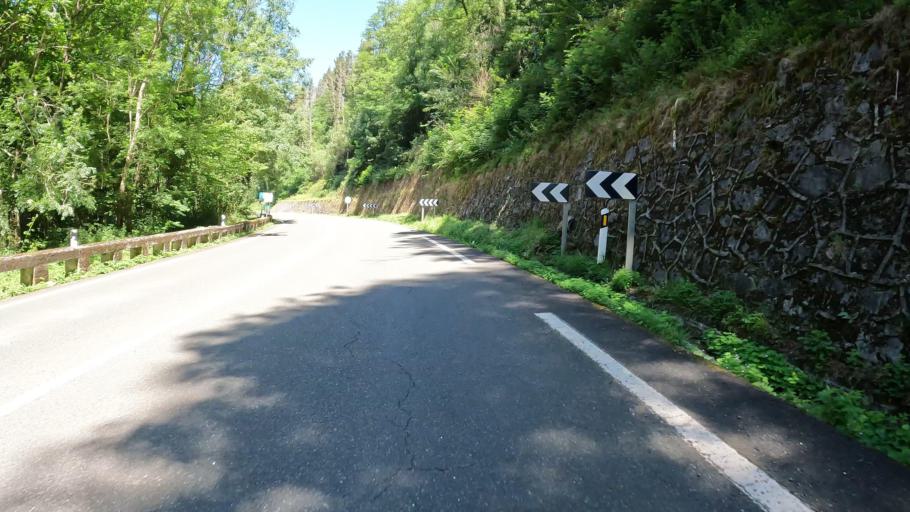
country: ES
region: Basque Country
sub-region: Provincia de Guipuzcoa
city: Oreja
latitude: 43.0741
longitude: -2.0120
